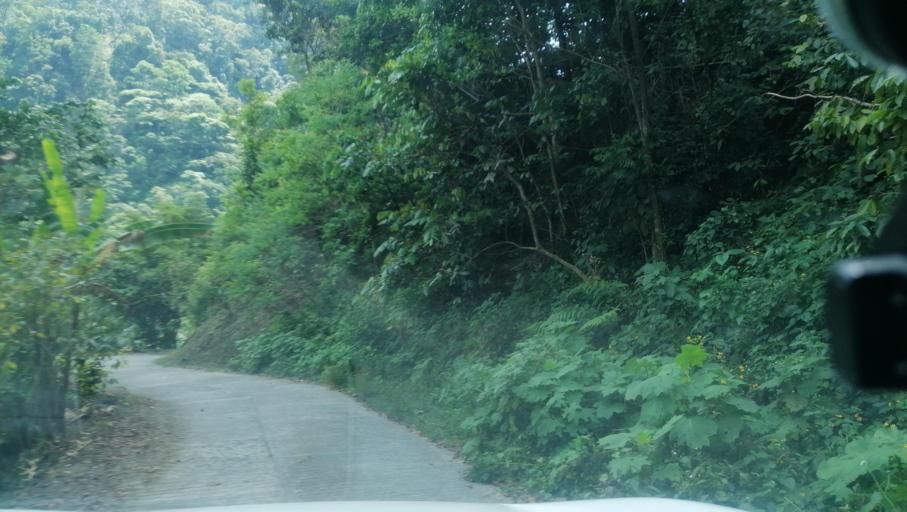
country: MX
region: Chiapas
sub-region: Union Juarez
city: Santo Domingo
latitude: 15.0747
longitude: -92.1302
